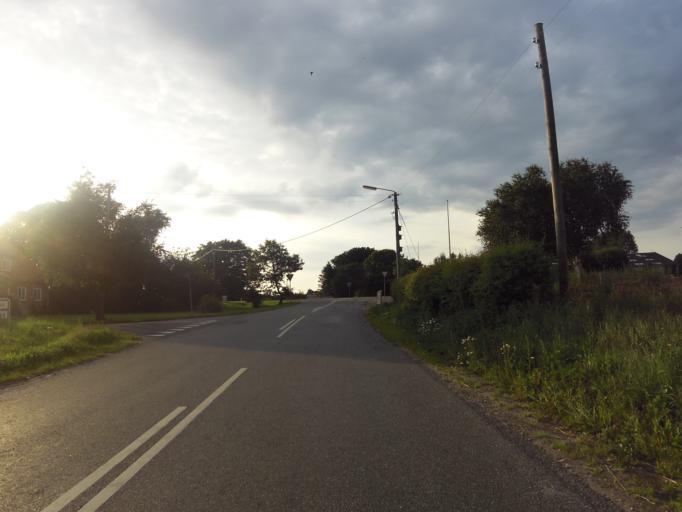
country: DK
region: South Denmark
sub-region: Tonder Kommune
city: Sherrebek
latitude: 55.2106
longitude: 8.8854
